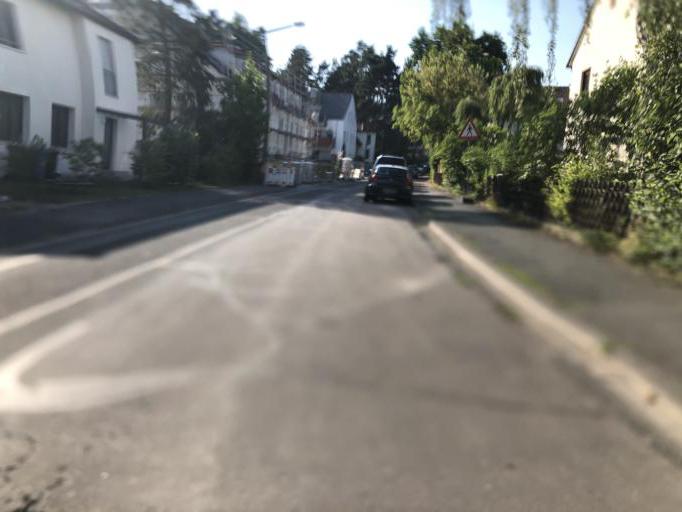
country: DE
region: Bavaria
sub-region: Regierungsbezirk Mittelfranken
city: Erlangen
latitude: 49.6054
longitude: 10.9767
